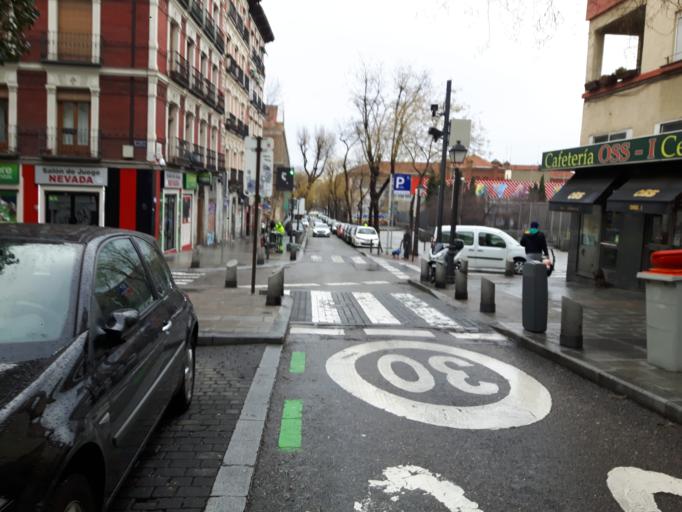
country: ES
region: Madrid
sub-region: Provincia de Madrid
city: Madrid
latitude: 40.4074
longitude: -3.7040
